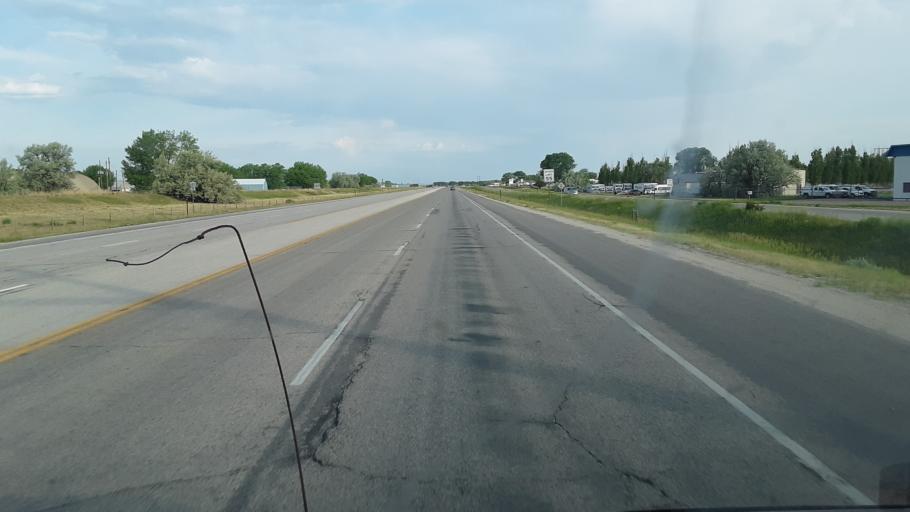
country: US
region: Wyoming
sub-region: Natrona County
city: Mills
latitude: 42.8797
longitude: -106.4352
